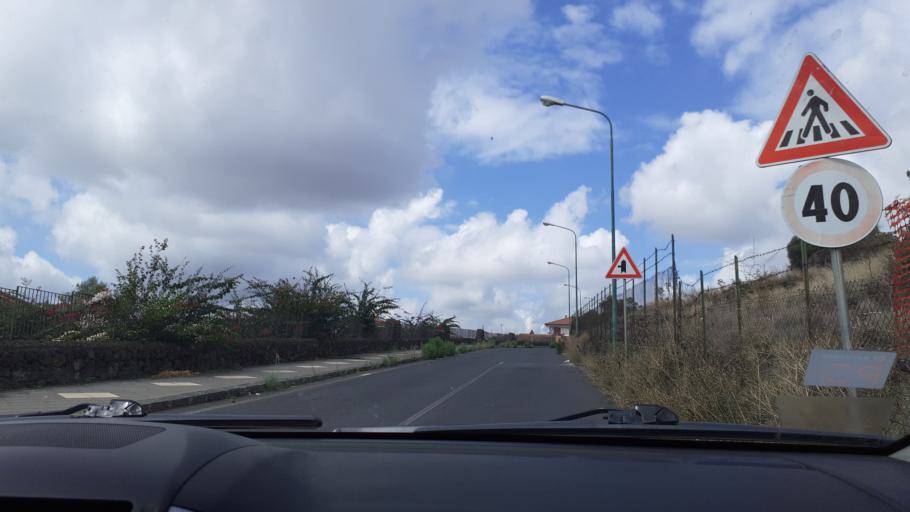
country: IT
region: Sicily
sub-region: Catania
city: Carrubazza-Motta
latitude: 37.5580
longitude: 15.1080
